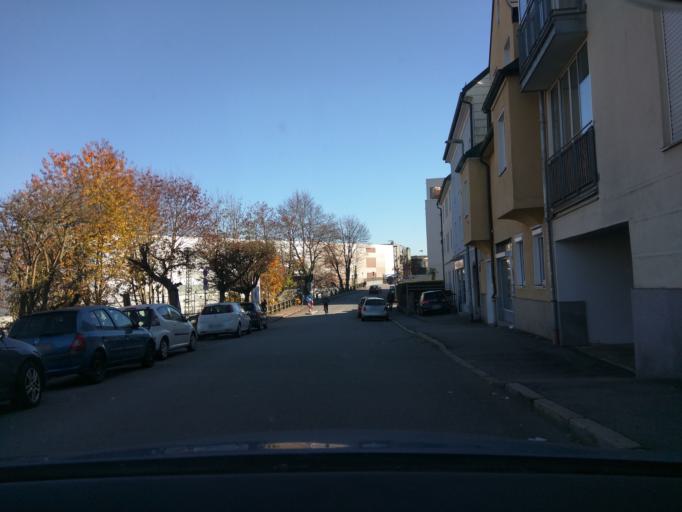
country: DE
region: Bavaria
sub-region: Lower Bavaria
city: Passau
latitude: 48.5732
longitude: 13.4533
